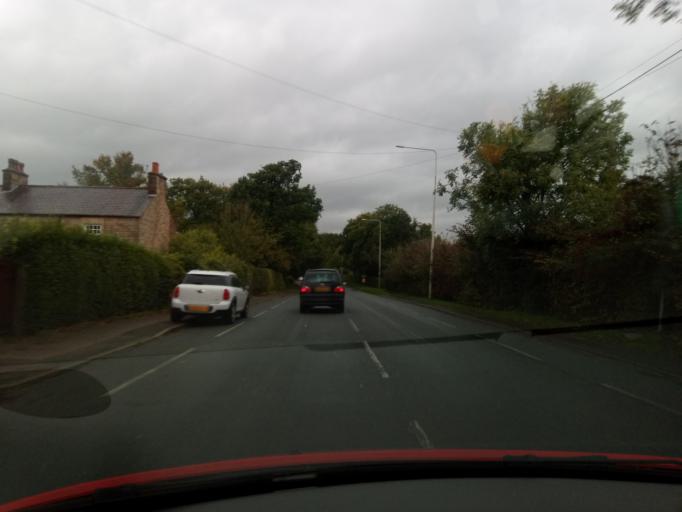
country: GB
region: England
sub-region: Lancashire
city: Catterall
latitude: 53.8393
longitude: -2.7398
